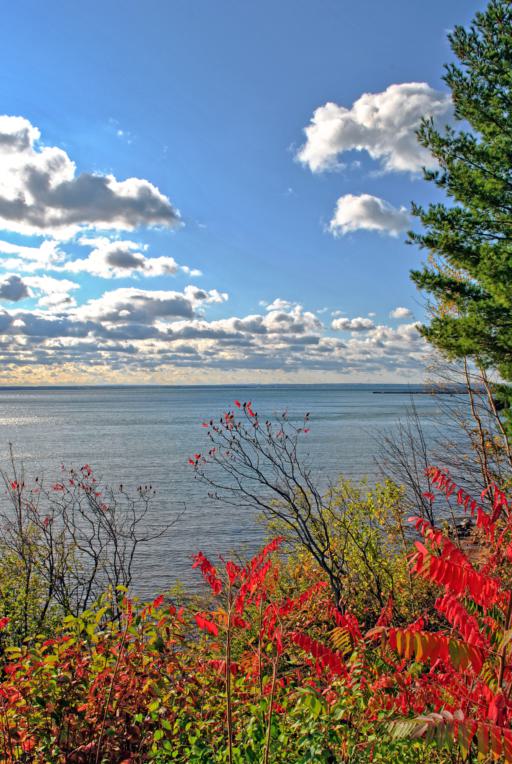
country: US
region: Wisconsin
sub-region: Bayfield County
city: Washburn
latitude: 46.6754
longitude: -90.8812
